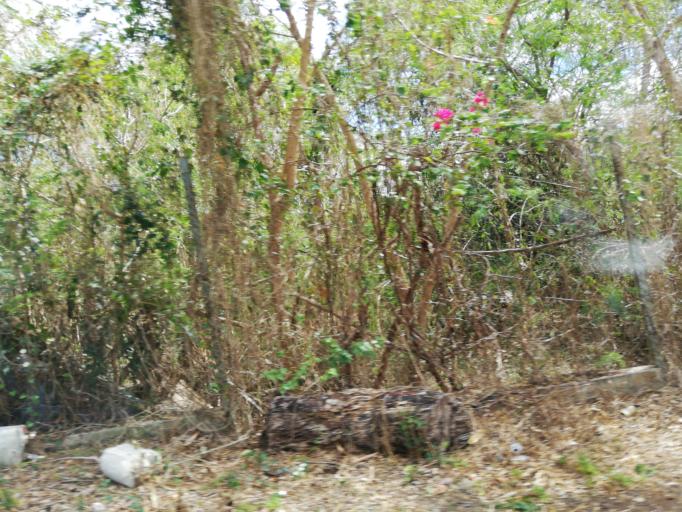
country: MU
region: Moka
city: Pailles
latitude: -20.1934
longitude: 57.4724
